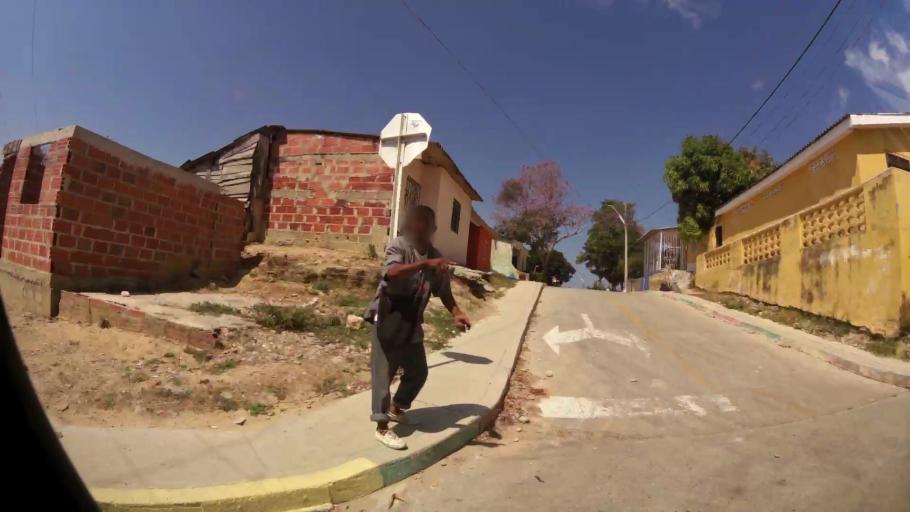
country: CO
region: Atlantico
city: Barranquilla
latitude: 10.9657
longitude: -74.8210
